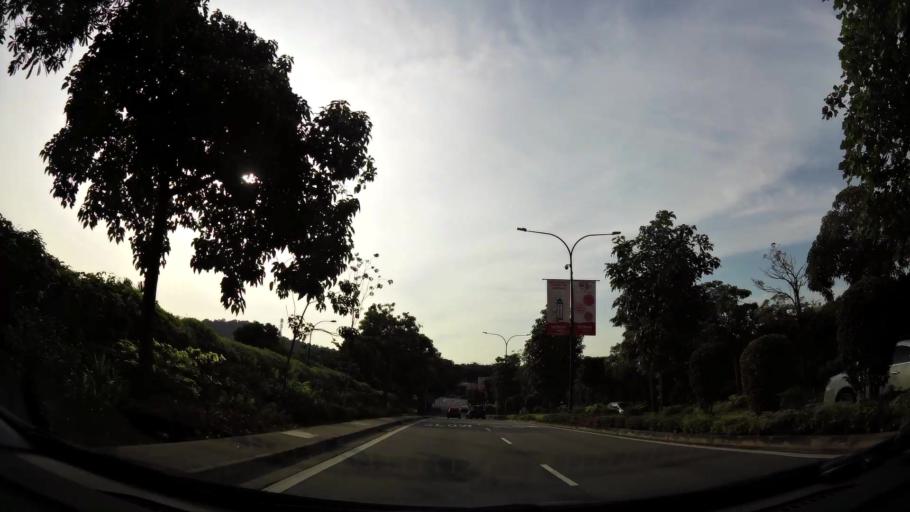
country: SG
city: Singapore
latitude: 1.2547
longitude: 103.8252
